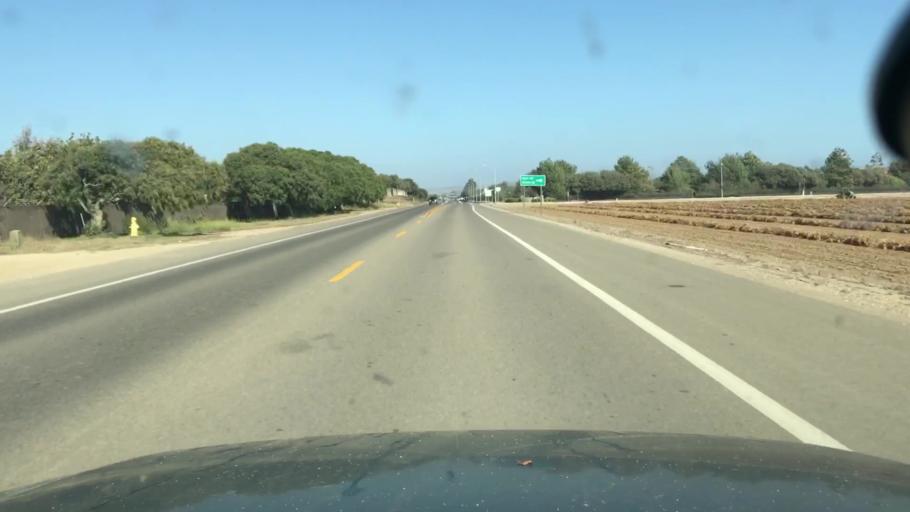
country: US
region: California
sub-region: Santa Barbara County
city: Lompoc
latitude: 34.6611
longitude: -120.4860
